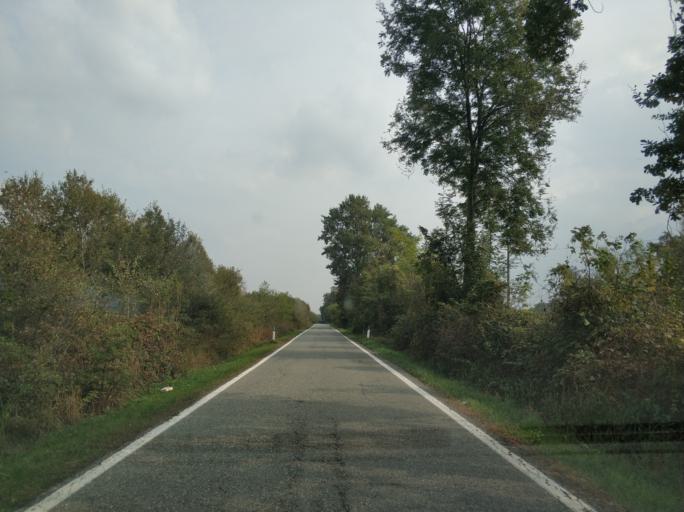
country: IT
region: Piedmont
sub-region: Provincia di Torino
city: San Francesco al Campo
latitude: 45.2417
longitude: 7.6802
